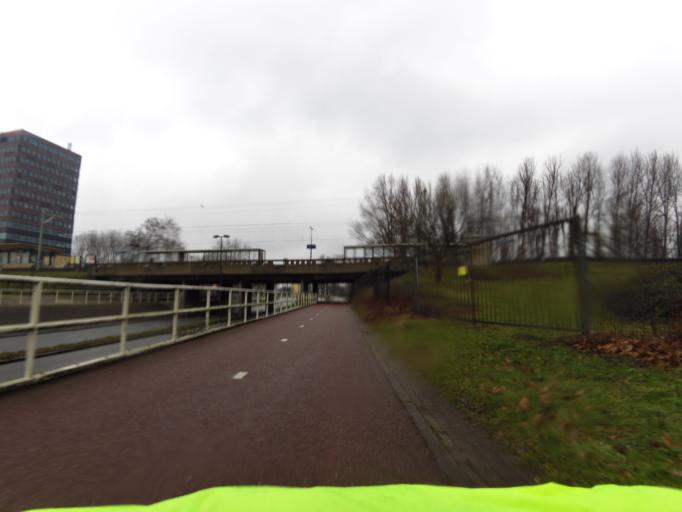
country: NL
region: South Holland
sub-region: Gemeente Vlaardingen
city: Vlaardingen
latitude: 51.9103
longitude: 4.3629
